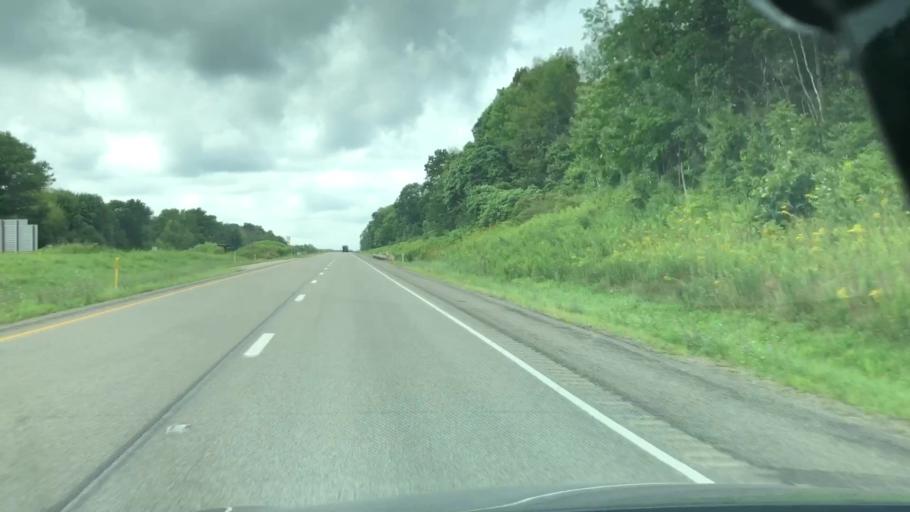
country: US
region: Pennsylvania
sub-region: Crawford County
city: Meadville
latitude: 41.6359
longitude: -80.1952
